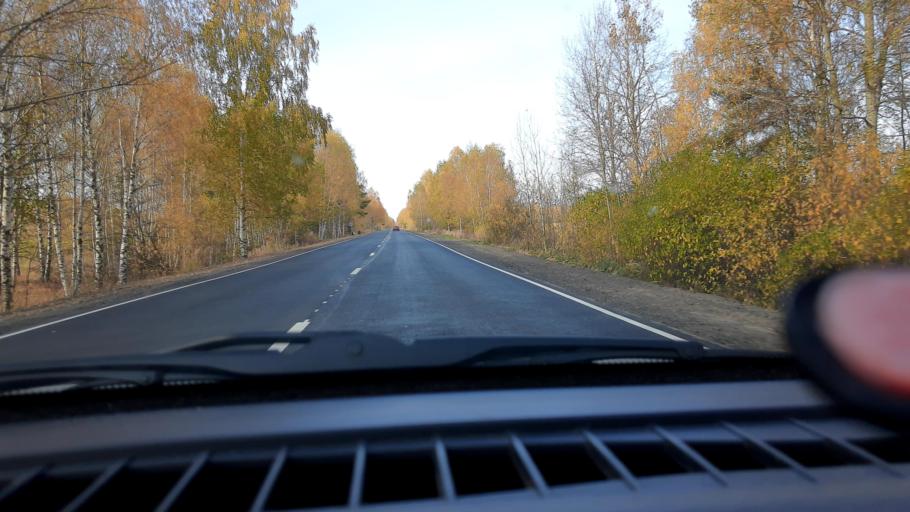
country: RU
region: Nizjnij Novgorod
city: Novaya Balakhna
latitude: 56.5515
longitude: 43.7480
